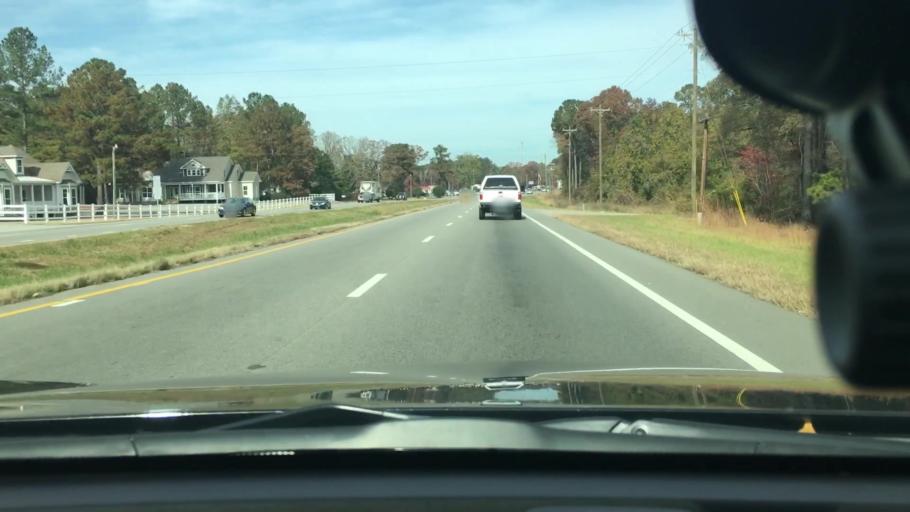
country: US
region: North Carolina
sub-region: Lee County
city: Sanford
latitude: 35.4068
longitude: -79.2316
